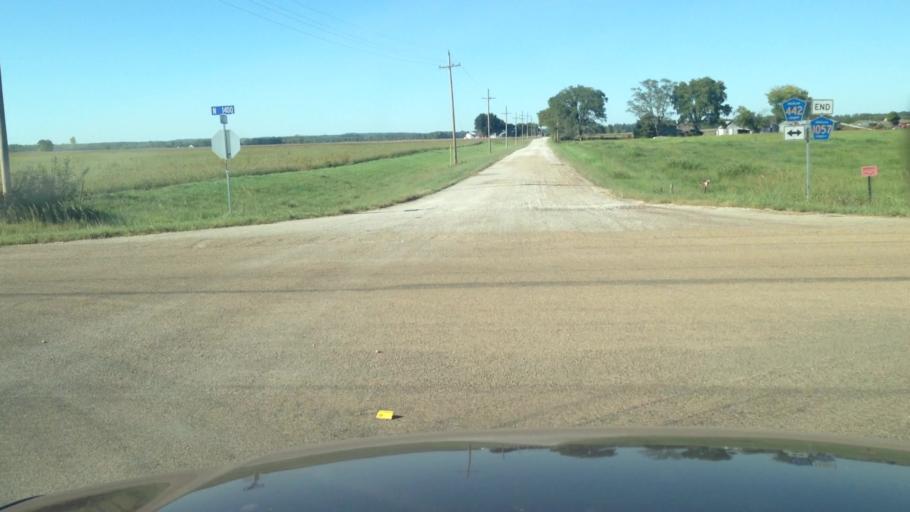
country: US
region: Kansas
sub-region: Douglas County
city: Eudora
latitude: 38.9423
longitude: -95.1489
